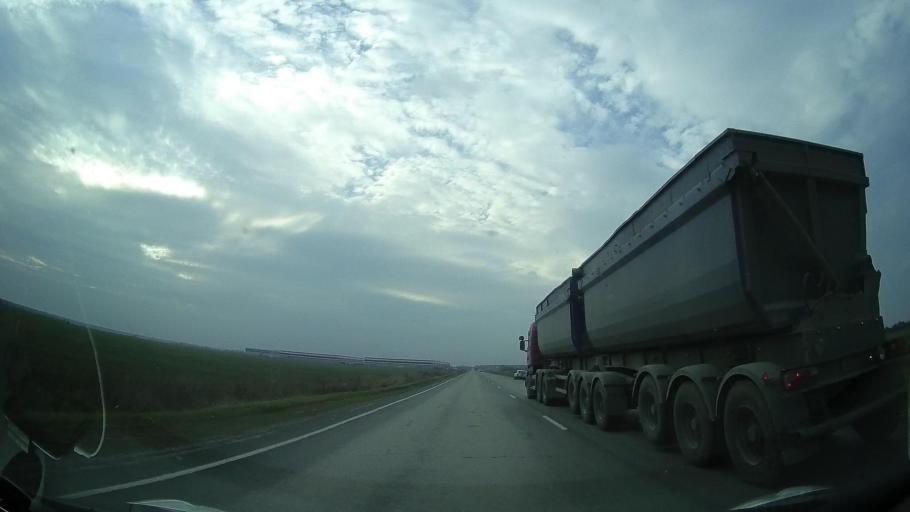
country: RU
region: Rostov
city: Ol'ginskaya
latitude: 47.1303
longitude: 39.9170
